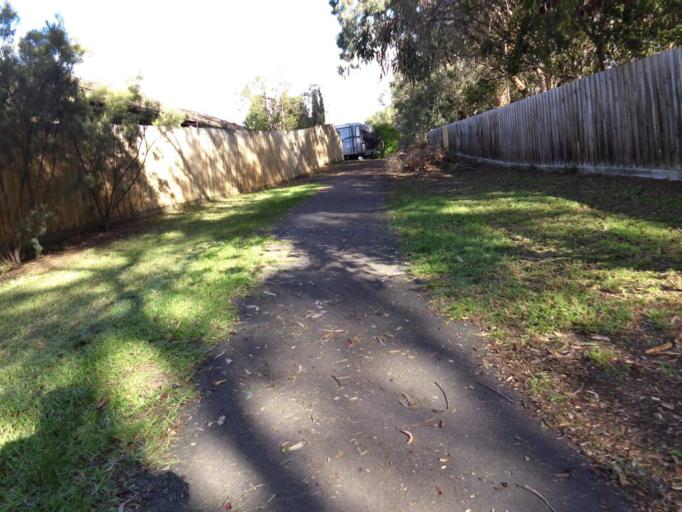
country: AU
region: Victoria
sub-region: Maroondah
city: Croydon Hills
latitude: -37.7742
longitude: 145.2620
